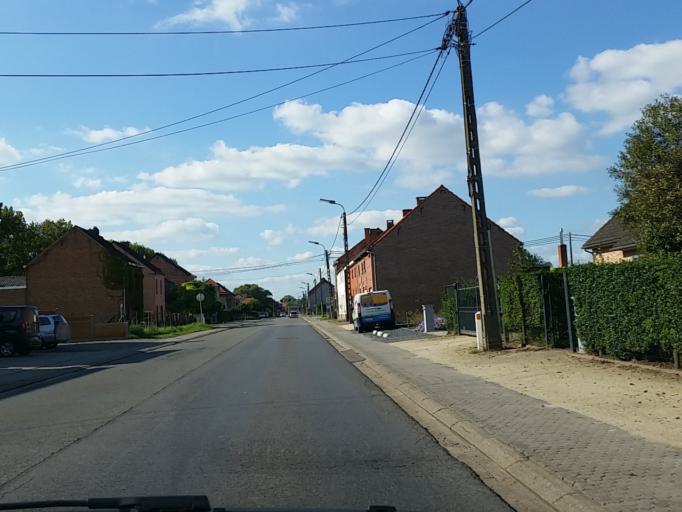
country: BE
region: Flanders
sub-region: Provincie Vlaams-Brabant
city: Rotselaar
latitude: 50.9474
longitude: 4.7205
